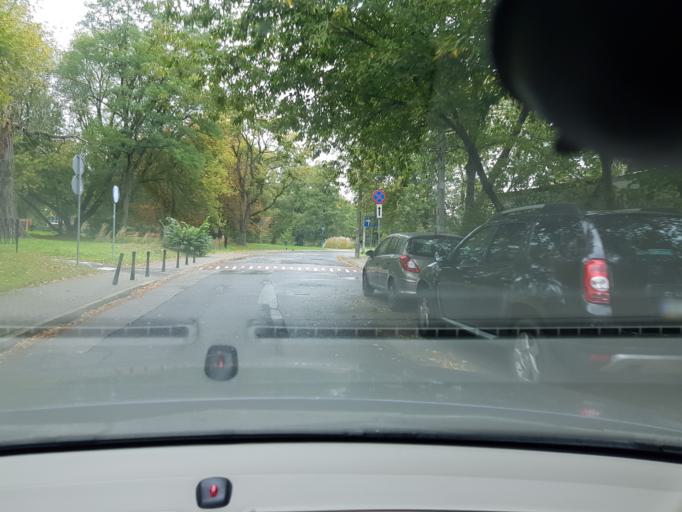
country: PL
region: Masovian Voivodeship
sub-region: Warszawa
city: Zoliborz
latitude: 52.2770
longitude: 20.9696
